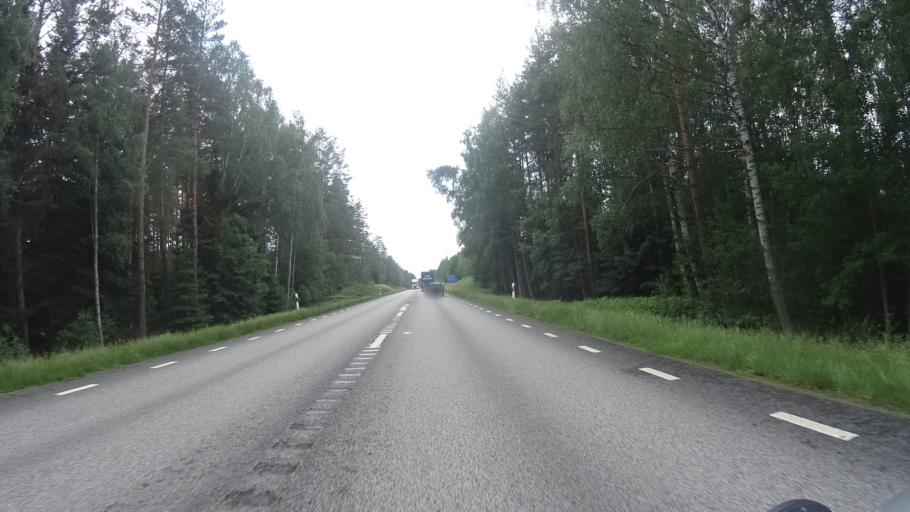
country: SE
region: Kalmar
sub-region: Hultsfreds Kommun
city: Hultsfred
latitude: 57.5388
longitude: 15.8457
